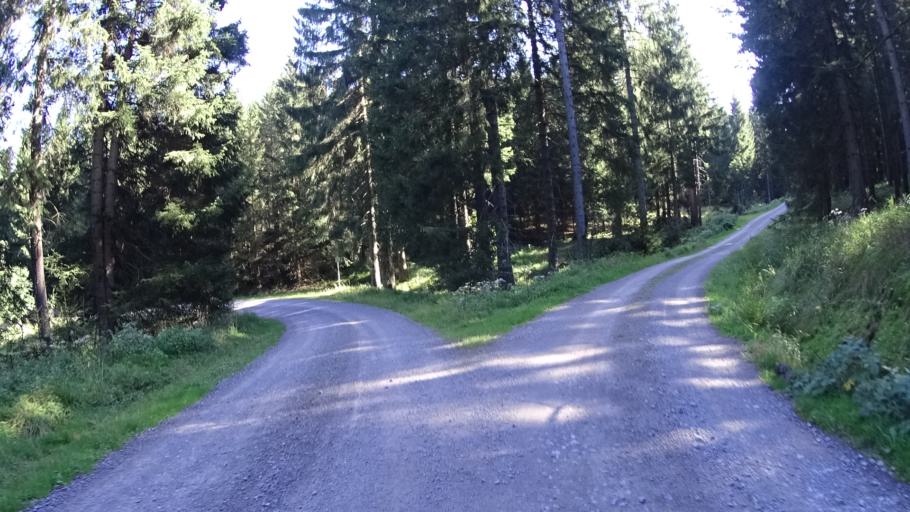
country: DE
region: Thuringia
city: Neustadt am Rennsteig
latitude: 50.6149
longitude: 10.9077
